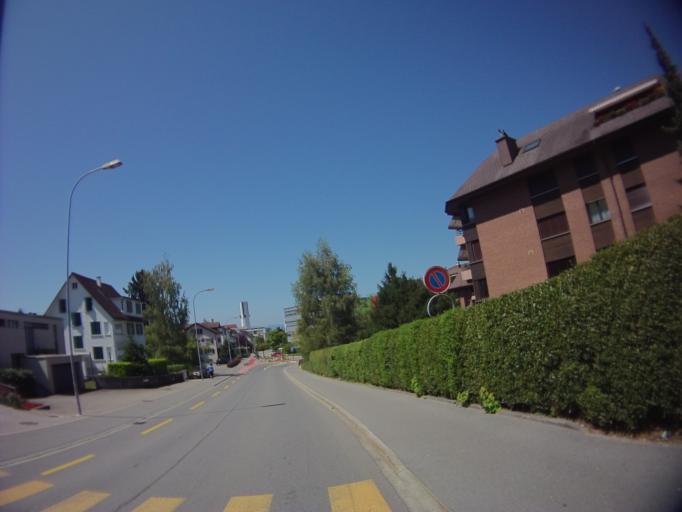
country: CH
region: Schwyz
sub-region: Bezirk Hoefe
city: Freienbach
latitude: 47.1992
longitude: 8.7823
